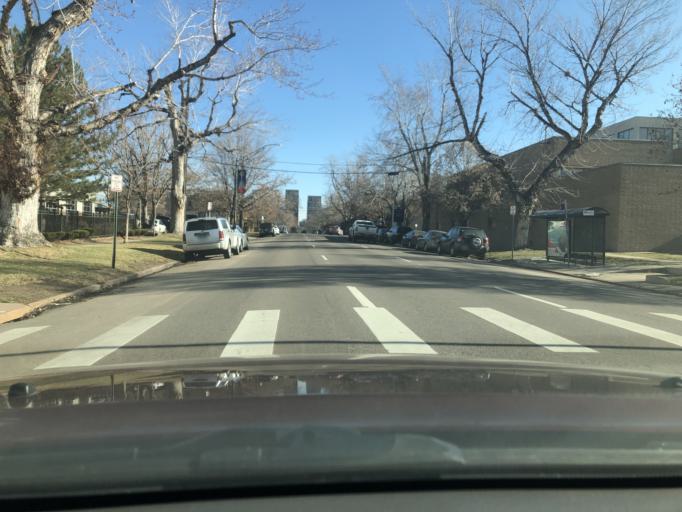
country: US
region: Colorado
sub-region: Denver County
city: Denver
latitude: 39.7433
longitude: -104.9660
